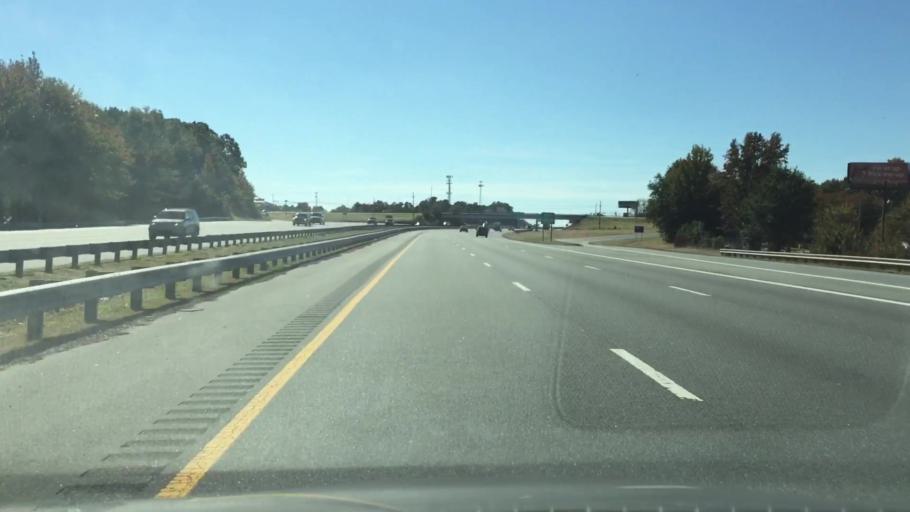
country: US
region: North Carolina
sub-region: Guilford County
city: Greensboro
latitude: 36.0139
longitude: -79.8353
